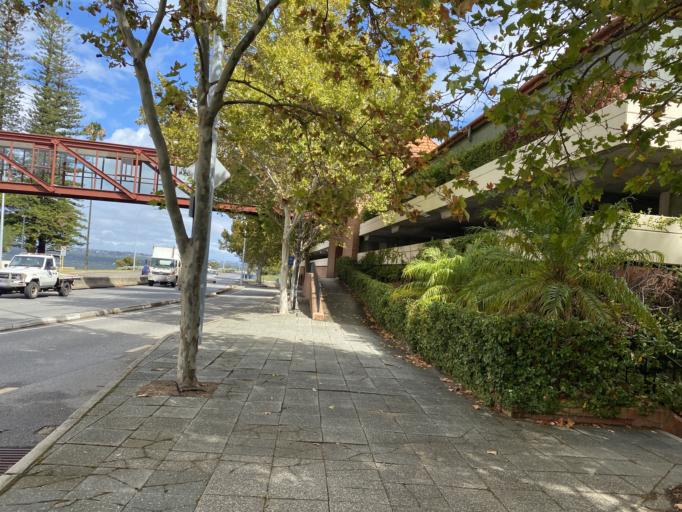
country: AU
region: Western Australia
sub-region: City of Perth
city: West Perth
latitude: -31.9650
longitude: 115.8400
